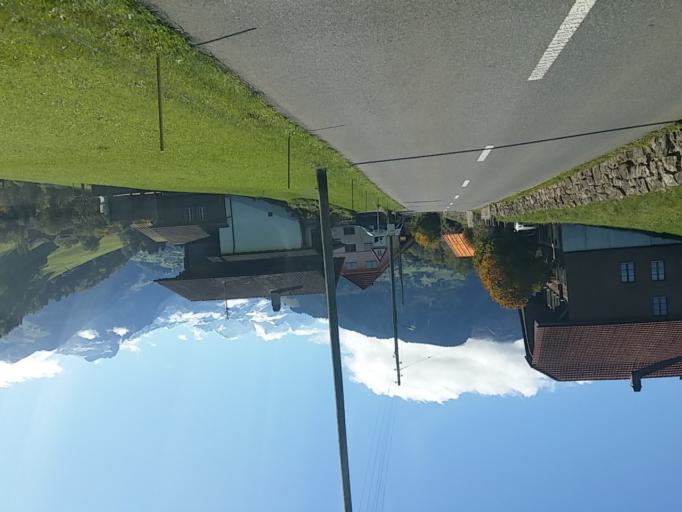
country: CH
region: Bern
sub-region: Frutigen-Niedersimmental District
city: Aeschi
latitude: 46.6560
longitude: 7.6827
